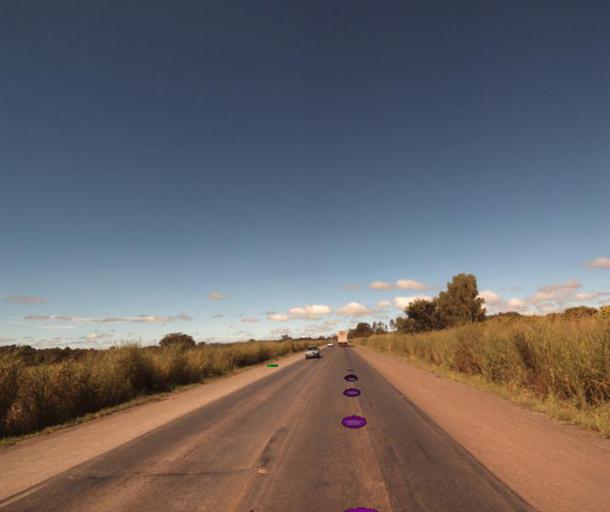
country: BR
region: Goias
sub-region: Itapaci
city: Itapaci
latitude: -15.0533
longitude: -49.4468
